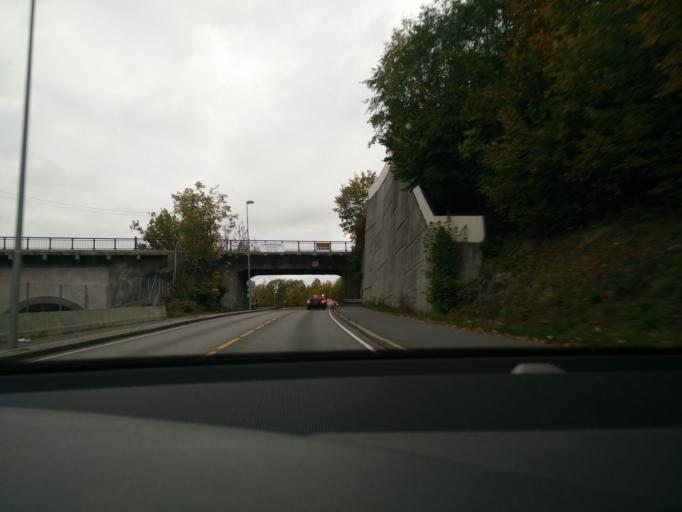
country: NO
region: Akershus
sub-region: Baerum
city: Lysaker
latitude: 59.9269
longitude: 10.6230
